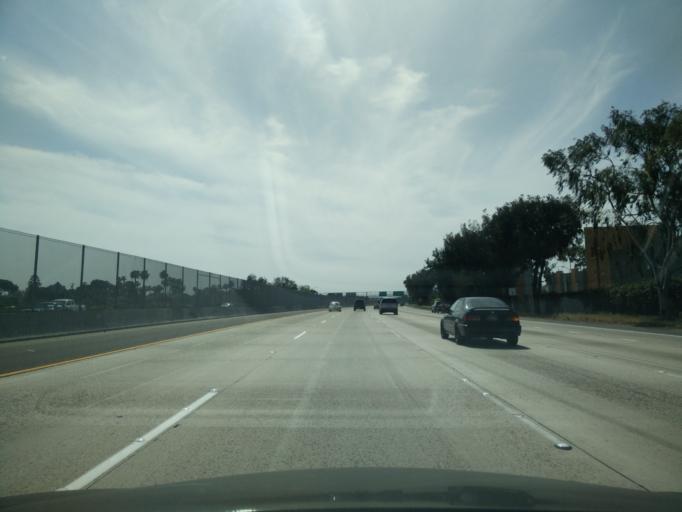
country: US
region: California
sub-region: San Diego County
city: Imperial Beach
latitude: 32.5760
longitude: -117.0820
